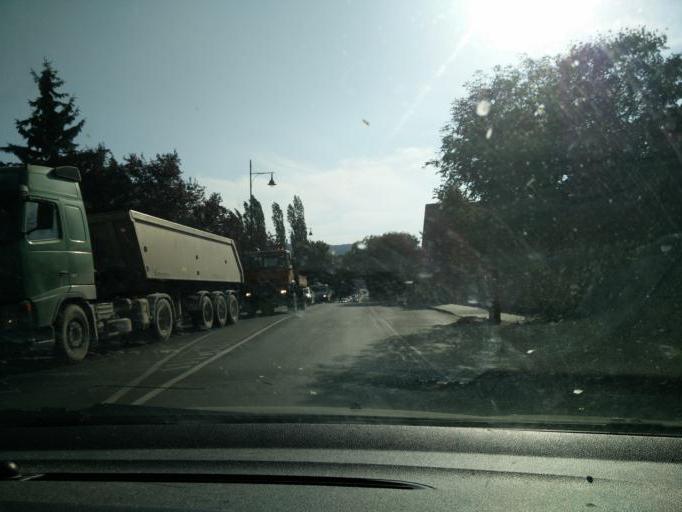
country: HU
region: Pest
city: Pilisvorosvar
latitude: 47.6182
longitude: 18.9045
